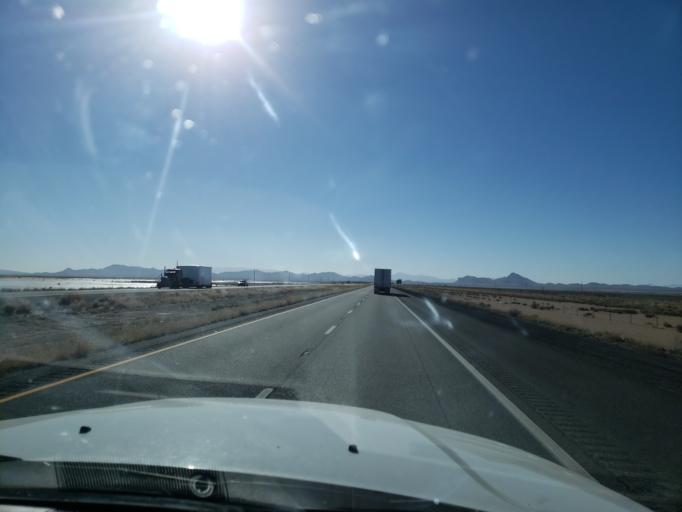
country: US
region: New Mexico
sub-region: Hidalgo County
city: Lordsburg
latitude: 32.2920
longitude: -108.8602
